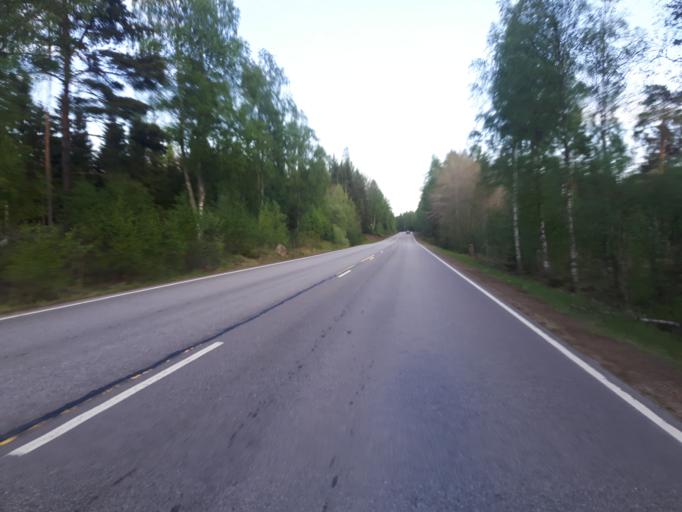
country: FI
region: Uusimaa
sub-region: Loviisa
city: Perna
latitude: 60.4603
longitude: 26.0503
